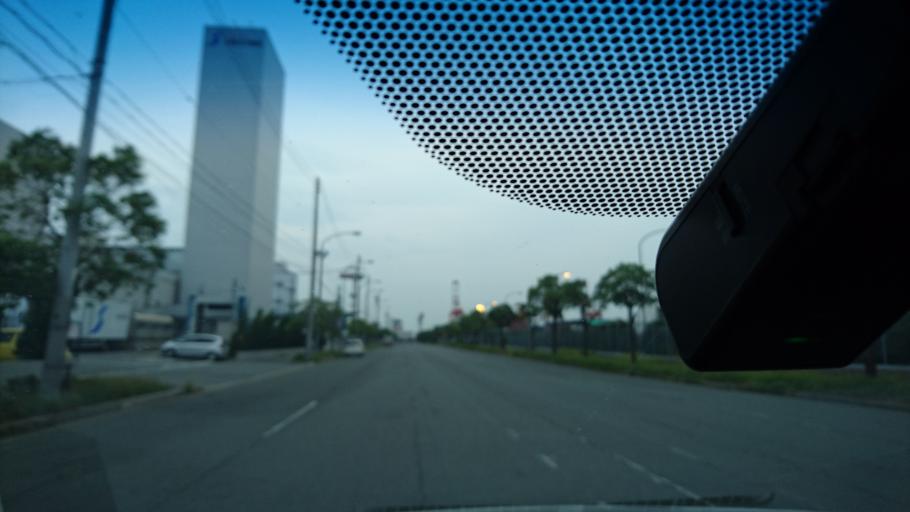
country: JP
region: Hyogo
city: Ashiya
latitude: 34.6864
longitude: 135.2574
